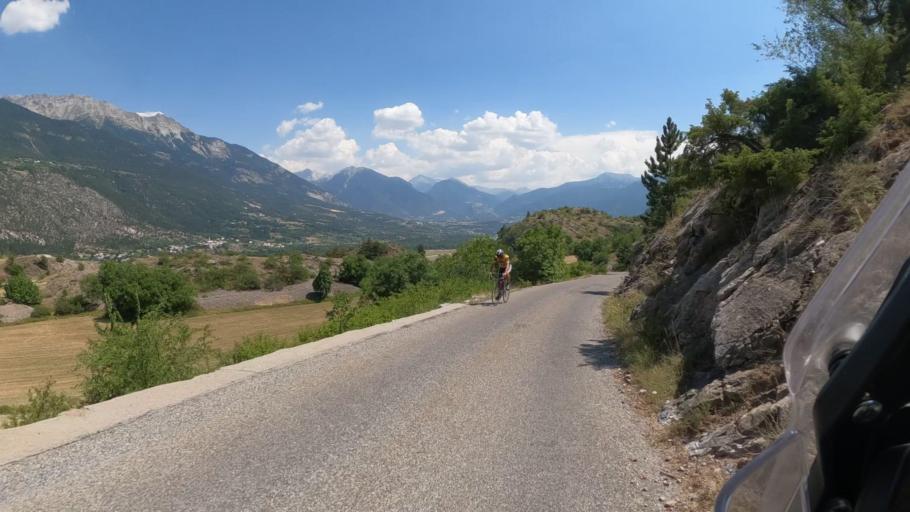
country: FR
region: Provence-Alpes-Cote d'Azur
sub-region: Departement des Hautes-Alpes
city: Guillestre
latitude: 44.7115
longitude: 6.5850
